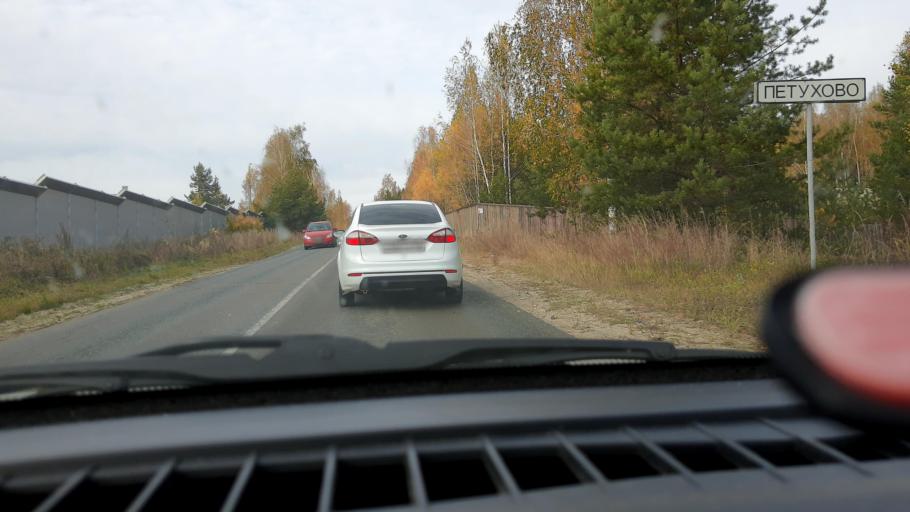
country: RU
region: Nizjnij Novgorod
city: Neklyudovo
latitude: 56.4398
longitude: 43.9112
